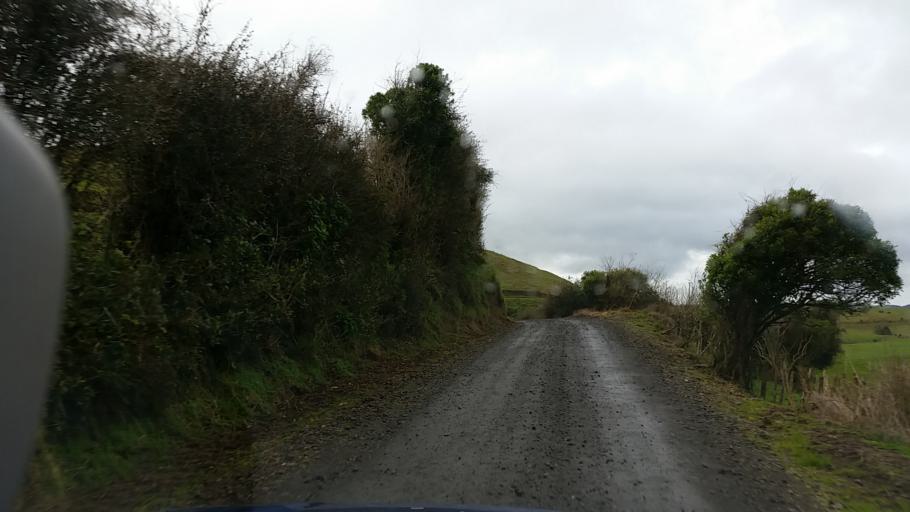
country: NZ
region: Taranaki
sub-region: South Taranaki District
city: Eltham
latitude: -39.2805
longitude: 174.3378
